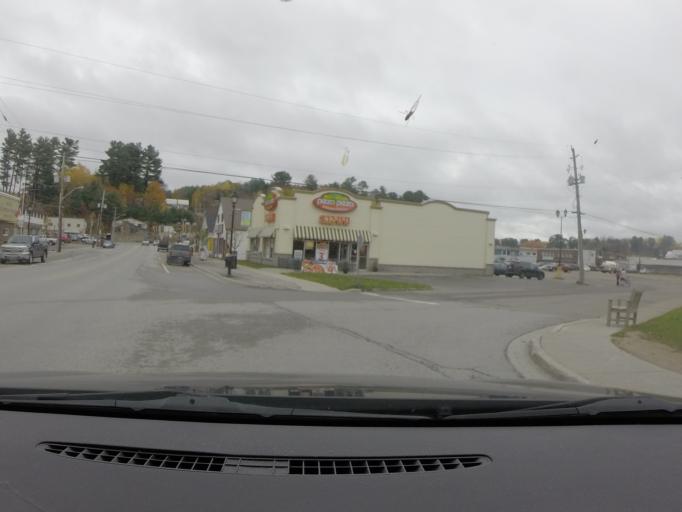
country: CA
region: Ontario
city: Bancroft
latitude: 45.0594
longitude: -77.8570
